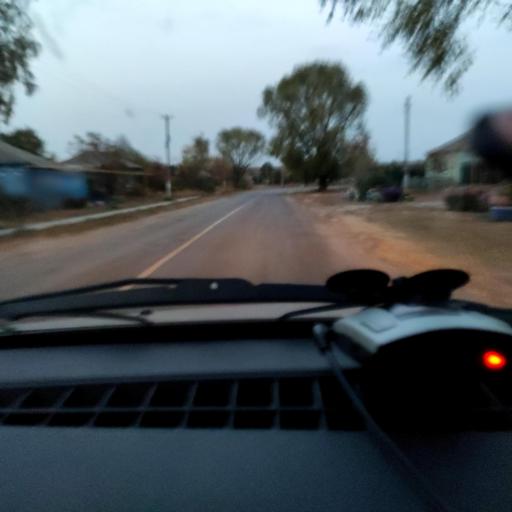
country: RU
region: Voronezj
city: Kolodeznyy
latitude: 51.2386
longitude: 39.0377
